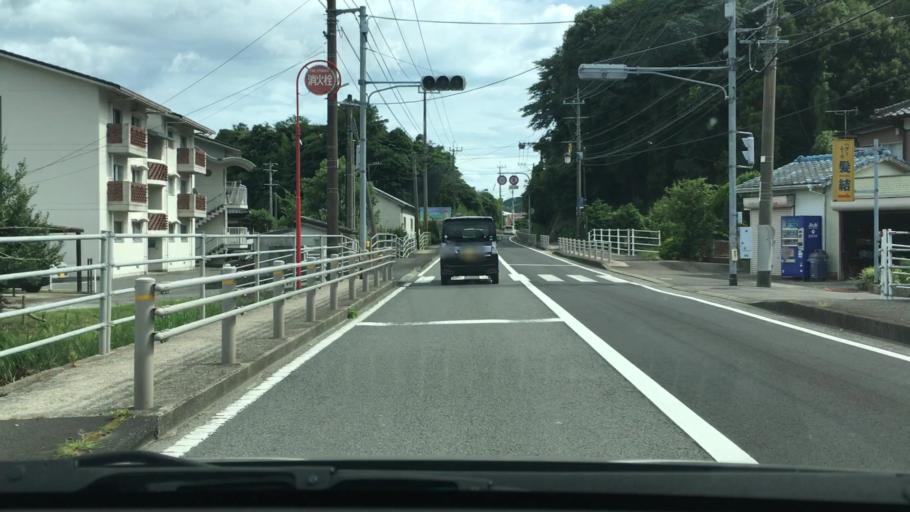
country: JP
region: Nagasaki
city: Togitsu
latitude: 32.9122
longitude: 129.7844
